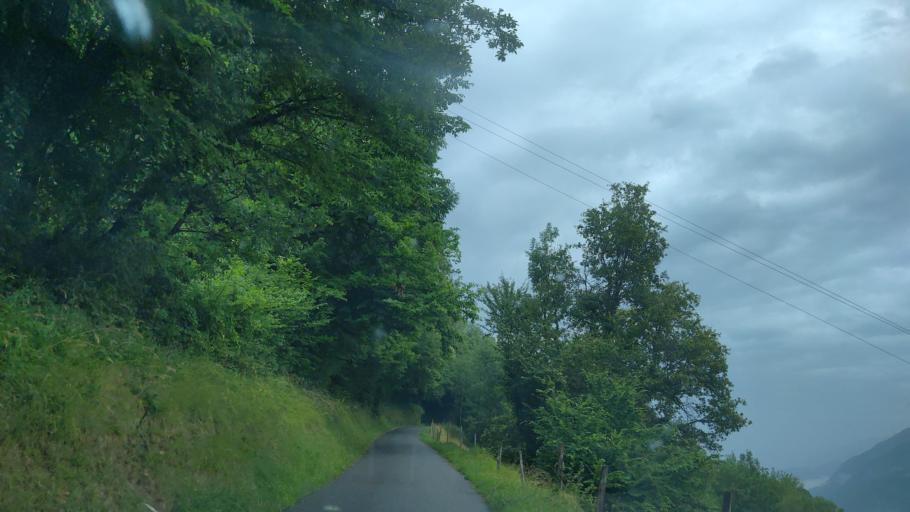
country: FR
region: Rhone-Alpes
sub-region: Departement de la Savoie
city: La Rochette
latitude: 45.4871
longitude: 6.1317
